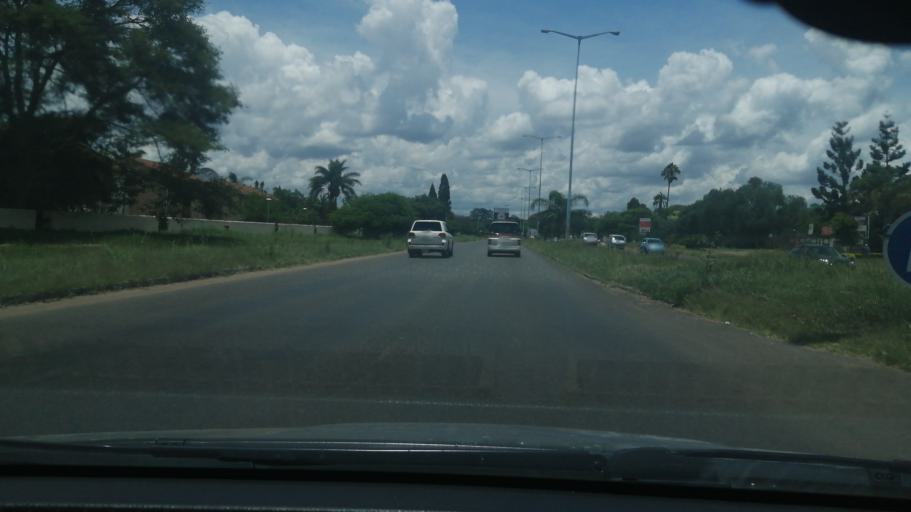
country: ZW
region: Harare
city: Harare
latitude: -17.8209
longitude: 31.0748
